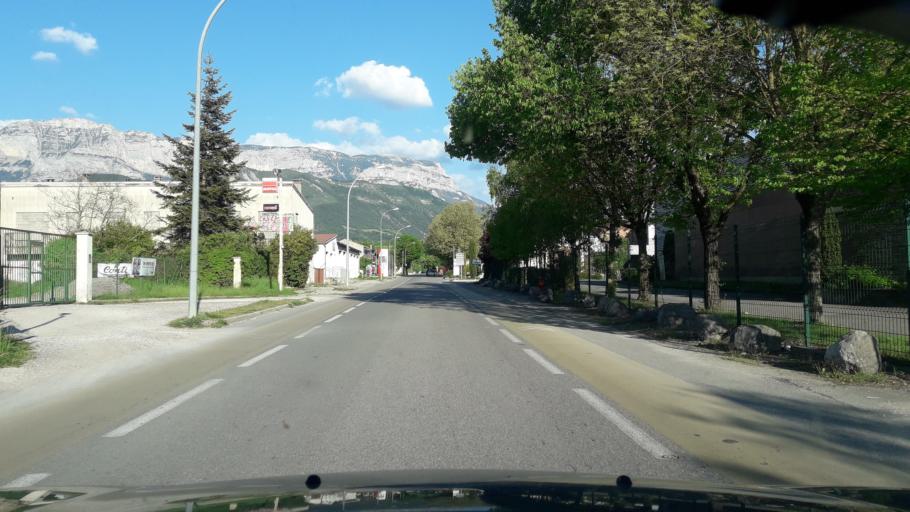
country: FR
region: Rhone-Alpes
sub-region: Departement de la Drome
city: Die
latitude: 44.7612
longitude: 5.3548
